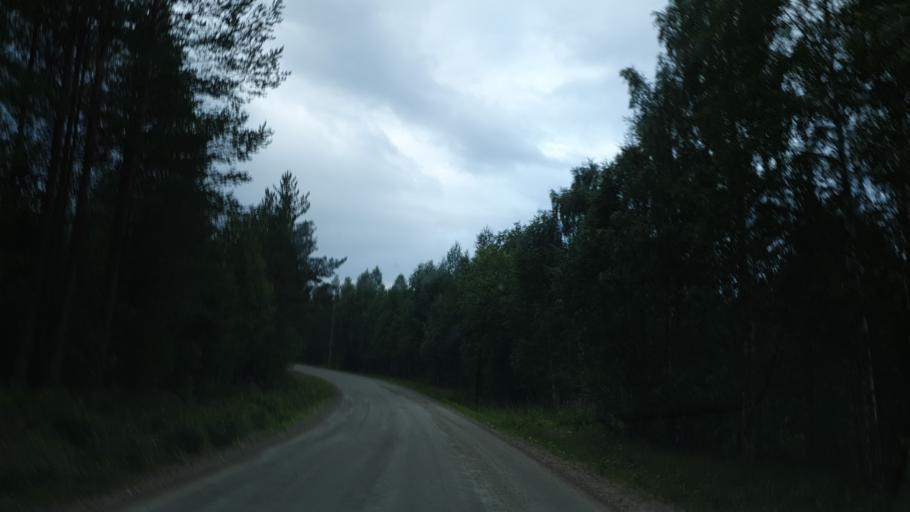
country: FI
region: Kainuu
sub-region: Kehys-Kainuu
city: Kuhmo
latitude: 64.1968
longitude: 29.3664
